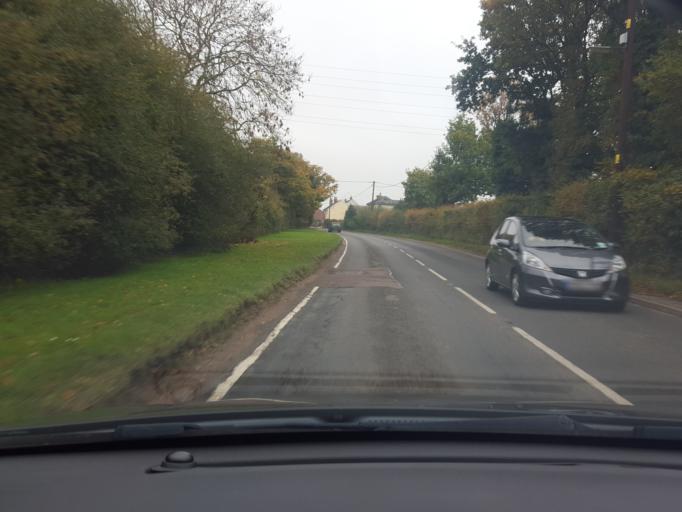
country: GB
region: England
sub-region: Essex
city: Great Bentley
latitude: 51.8459
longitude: 1.0338
